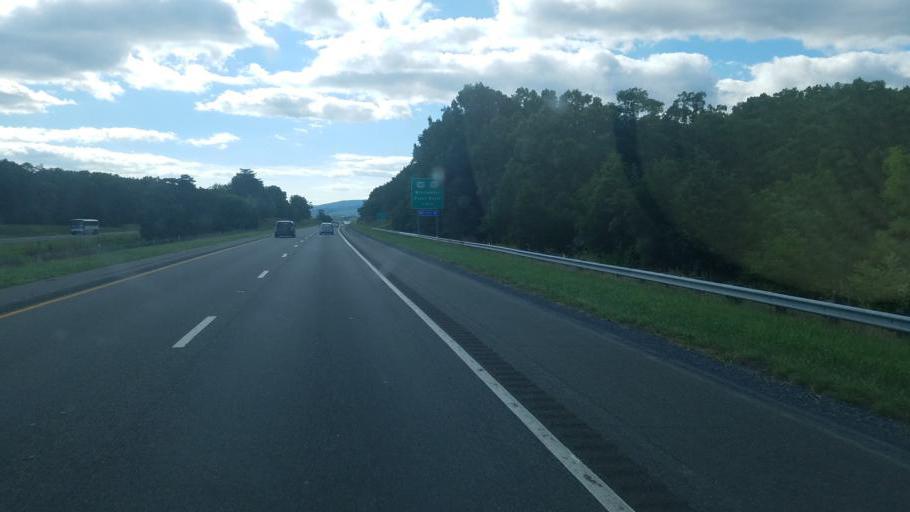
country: US
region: Virginia
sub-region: Warren County
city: Front Royal
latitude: 38.9718
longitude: -78.2106
